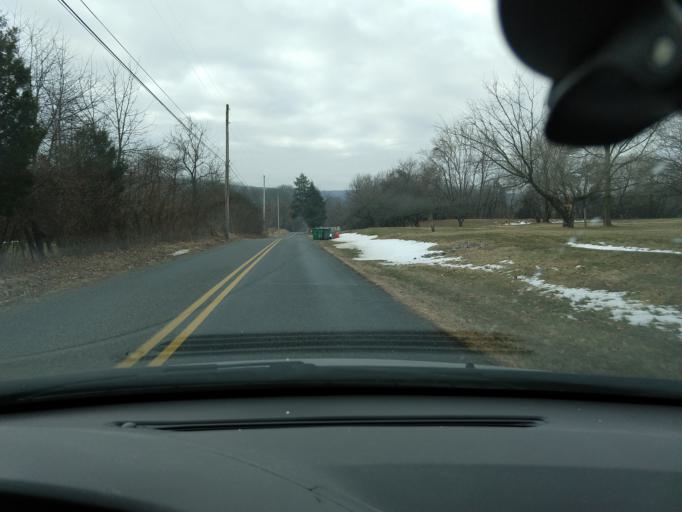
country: US
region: Pennsylvania
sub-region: Berks County
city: Amity Gardens
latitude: 40.2439
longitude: -75.7449
